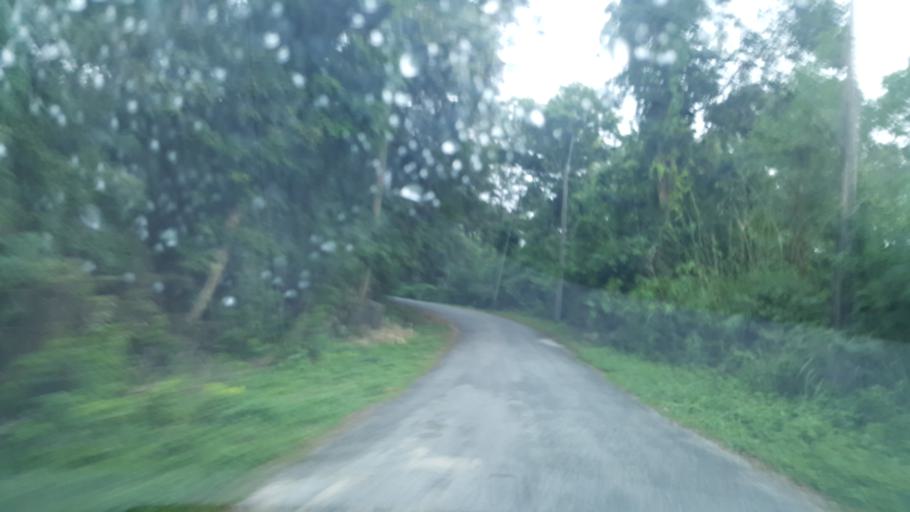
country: TH
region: Chon Buri
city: Ban Bueng
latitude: 13.2372
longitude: 101.0407
